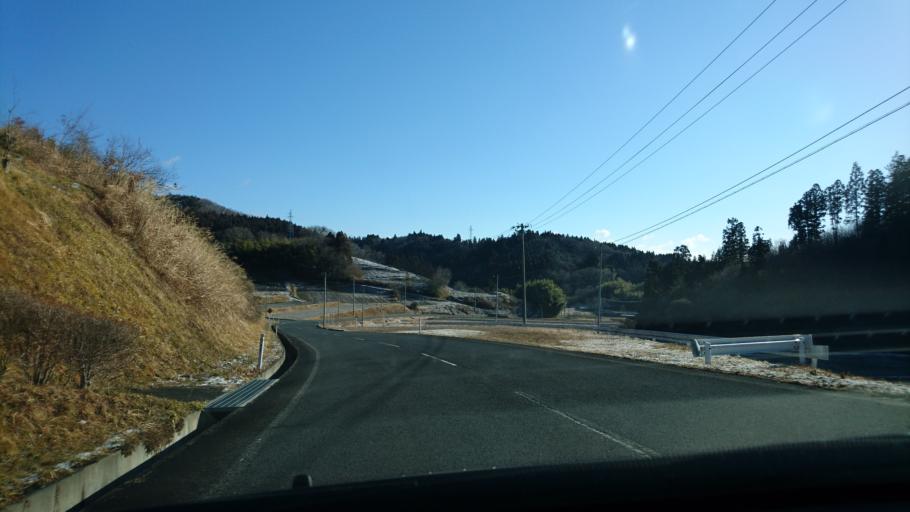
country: JP
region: Iwate
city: Ichinoseki
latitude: 38.8790
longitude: 141.3147
